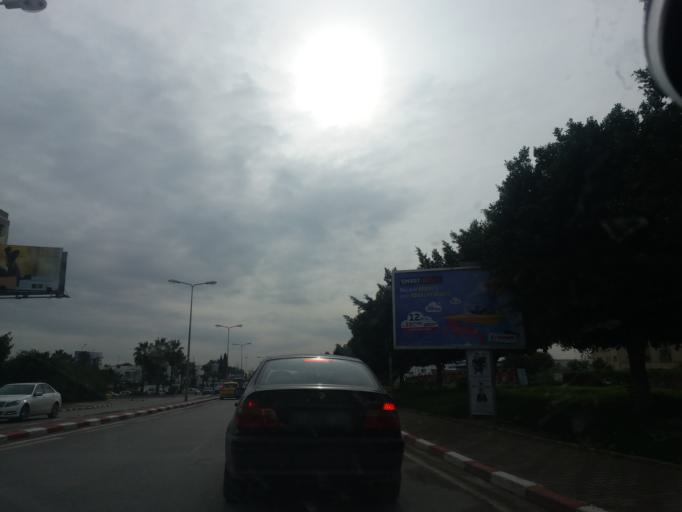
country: TN
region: Tunis
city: Tunis
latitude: 36.8441
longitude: 10.1642
